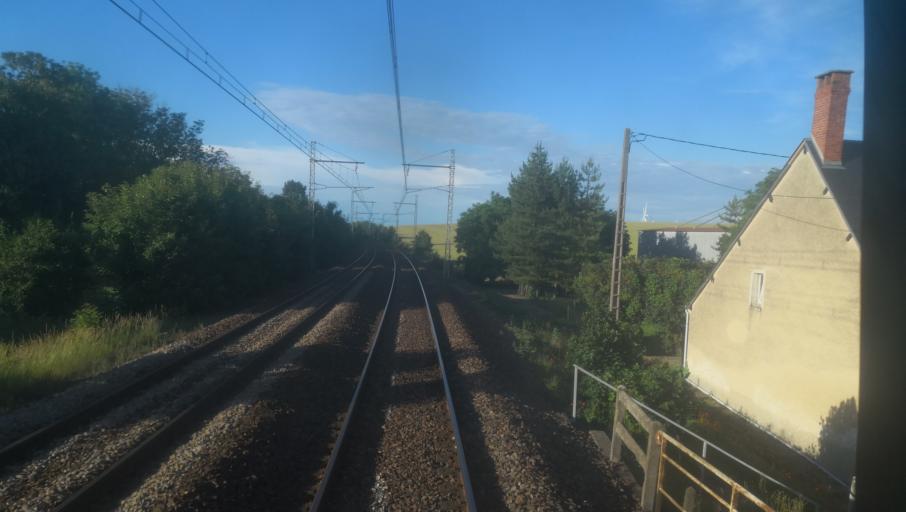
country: FR
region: Centre
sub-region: Departement de l'Indre
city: Sainte-Lizaigne
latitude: 46.9854
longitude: 2.0165
